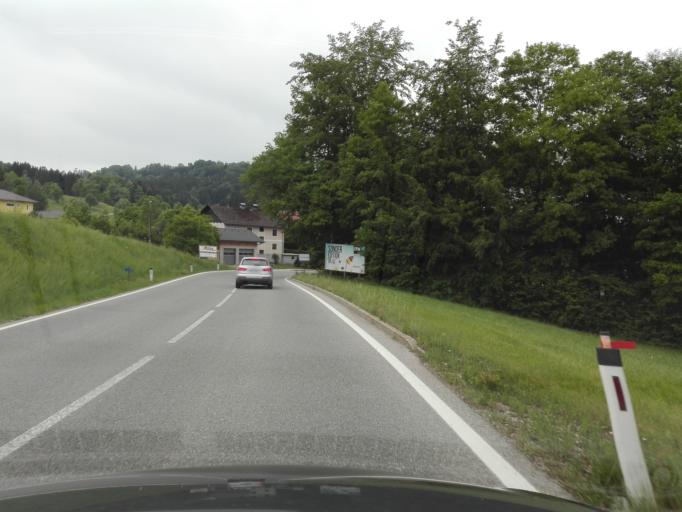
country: AT
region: Upper Austria
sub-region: Politischer Bezirk Gmunden
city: Gmunden
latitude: 47.9190
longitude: 13.8757
